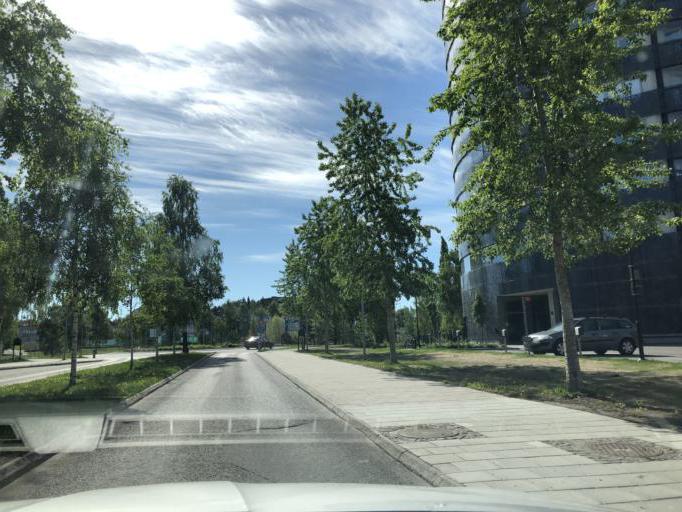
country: SE
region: Norrbotten
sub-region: Pitea Kommun
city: Pitea
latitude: 65.3159
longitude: 21.4887
